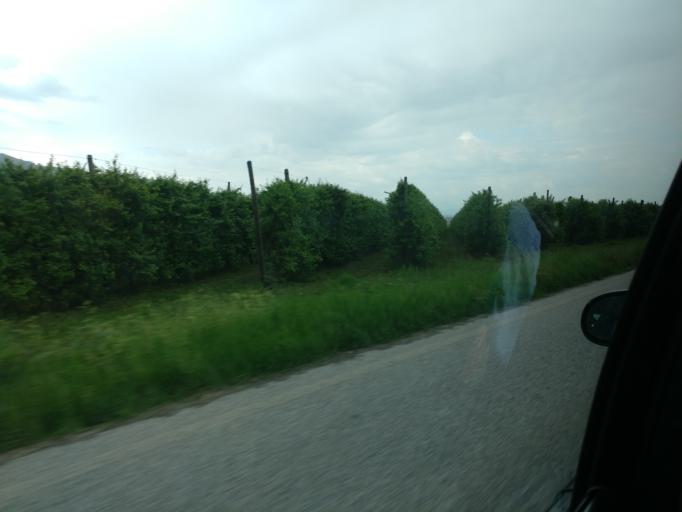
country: IT
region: Piedmont
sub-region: Provincia di Cuneo
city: Revello
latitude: 44.6662
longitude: 7.3965
